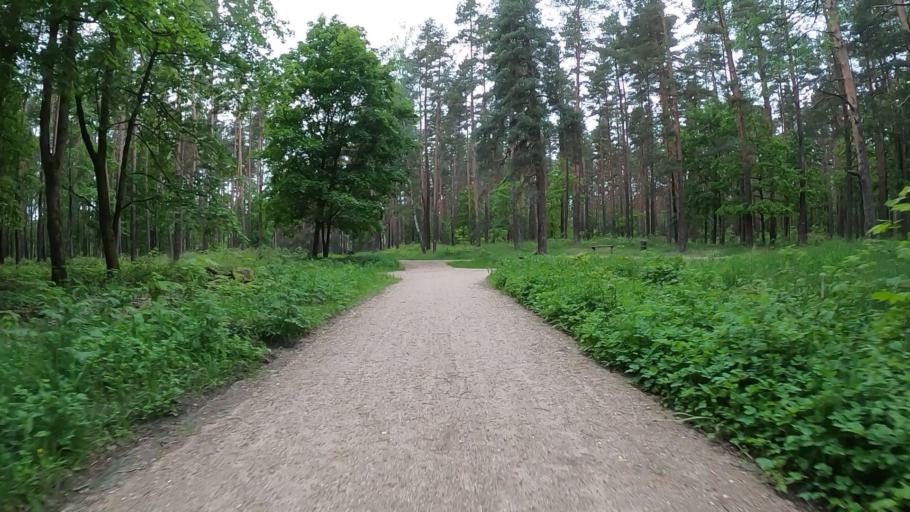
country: LV
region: Riga
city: Jaunciems
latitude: 56.9676
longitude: 24.2037
